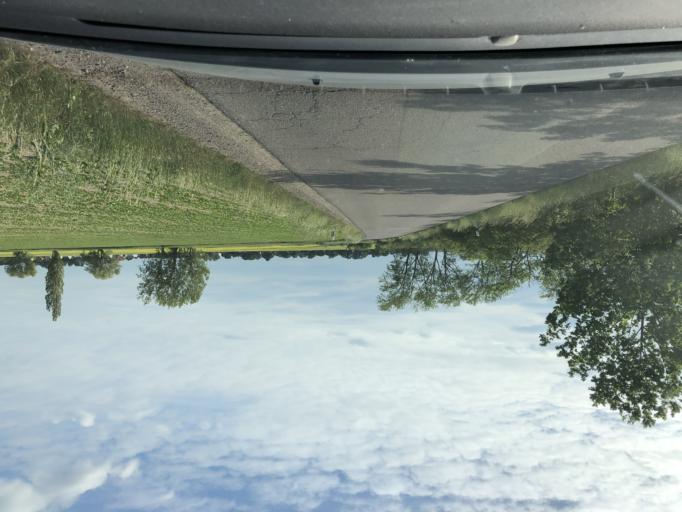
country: DE
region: Saxony
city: Borsdorf
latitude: 51.3295
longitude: 12.5278
